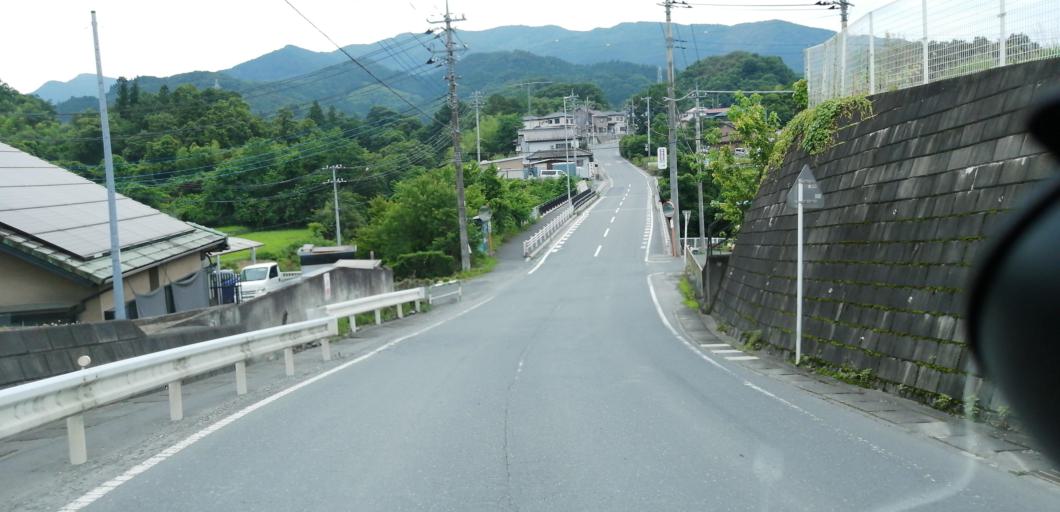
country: JP
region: Saitama
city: Chichibu
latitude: 36.0278
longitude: 139.1151
